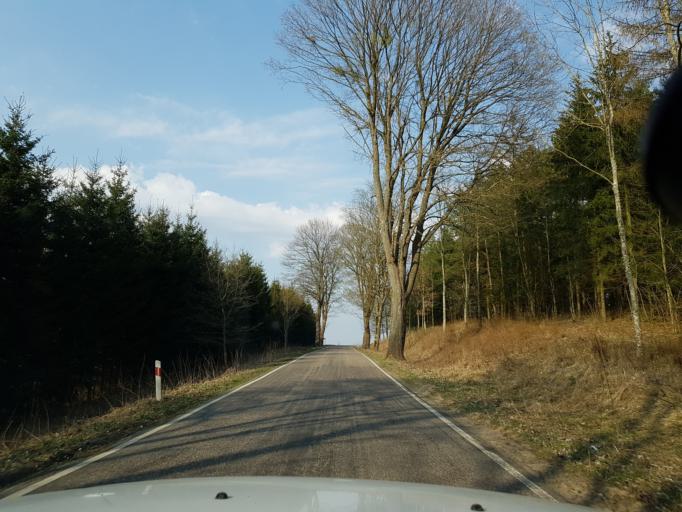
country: PL
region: West Pomeranian Voivodeship
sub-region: Powiat drawski
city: Drawsko Pomorskie
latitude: 53.5881
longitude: 15.8892
